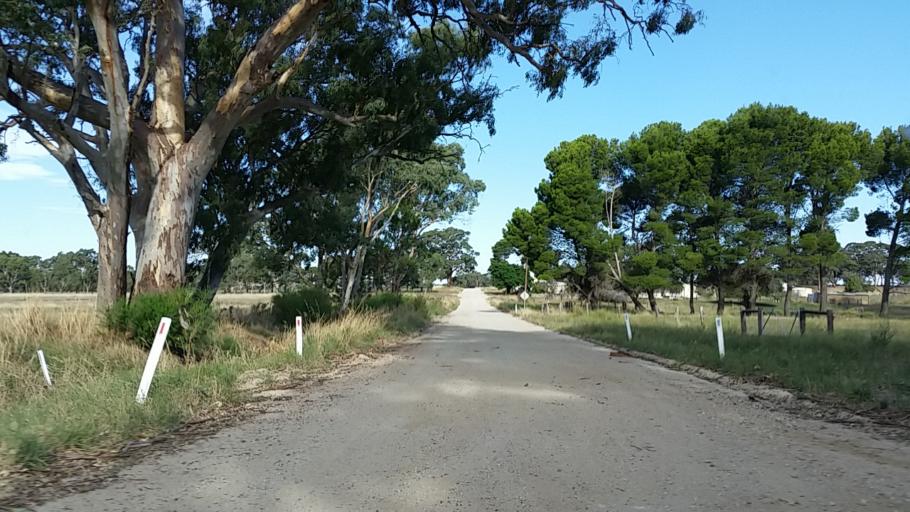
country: AU
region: South Australia
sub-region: Barossa
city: Angaston
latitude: -34.5817
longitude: 139.1494
